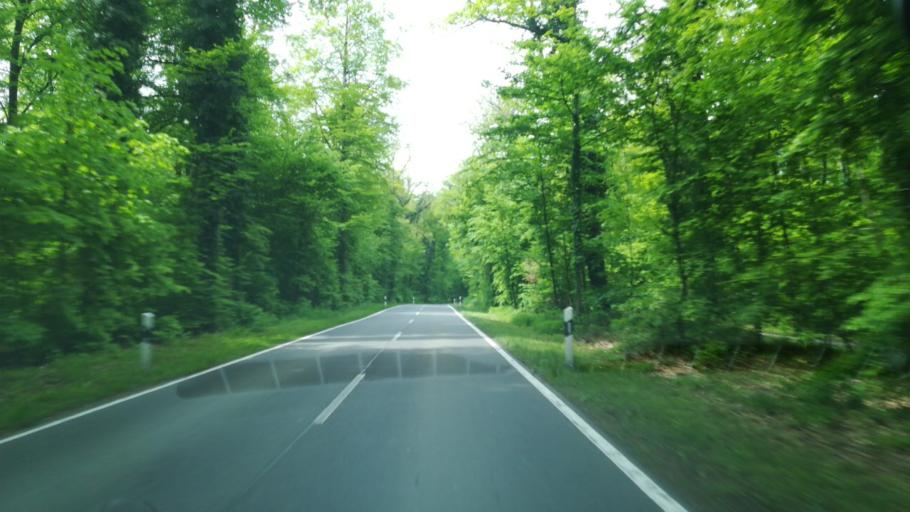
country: DE
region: Baden-Wuerttemberg
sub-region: Freiburg Region
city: Singen
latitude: 47.7732
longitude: 8.8606
